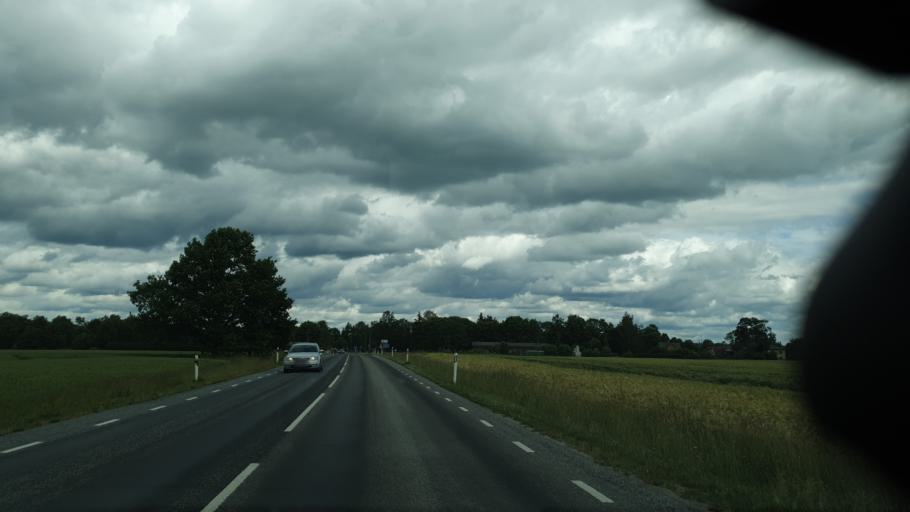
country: EE
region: Jaervamaa
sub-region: Jaerva-Jaani vald
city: Jarva-Jaani
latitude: 59.1859
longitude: 25.7643
